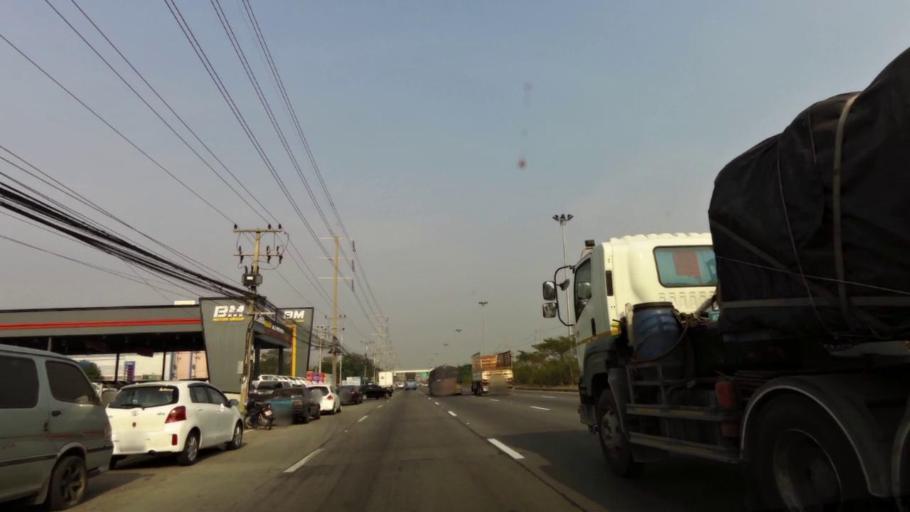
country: TH
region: Phra Nakhon Si Ayutthaya
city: Phra Nakhon Si Ayutthaya
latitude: 14.3280
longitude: 100.6253
